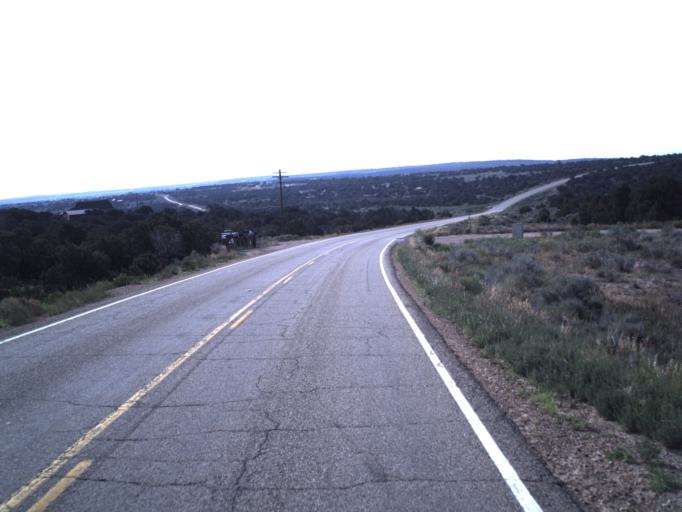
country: US
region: Utah
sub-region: Duchesne County
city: Duchesne
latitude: 40.3120
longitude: -110.3785
